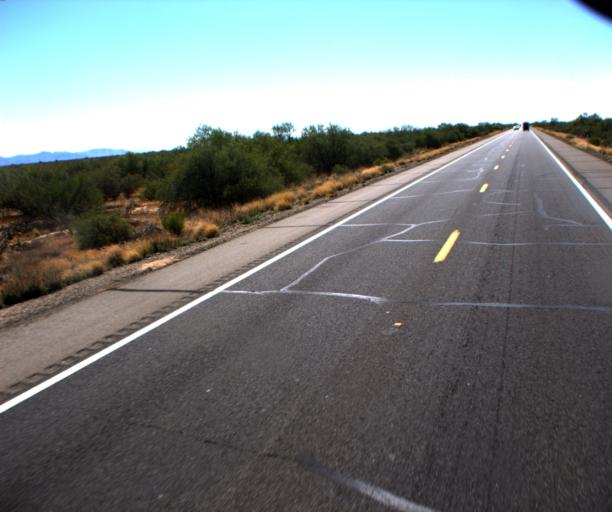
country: US
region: Arizona
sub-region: Yavapai County
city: Congress
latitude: 34.1586
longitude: -113.0012
